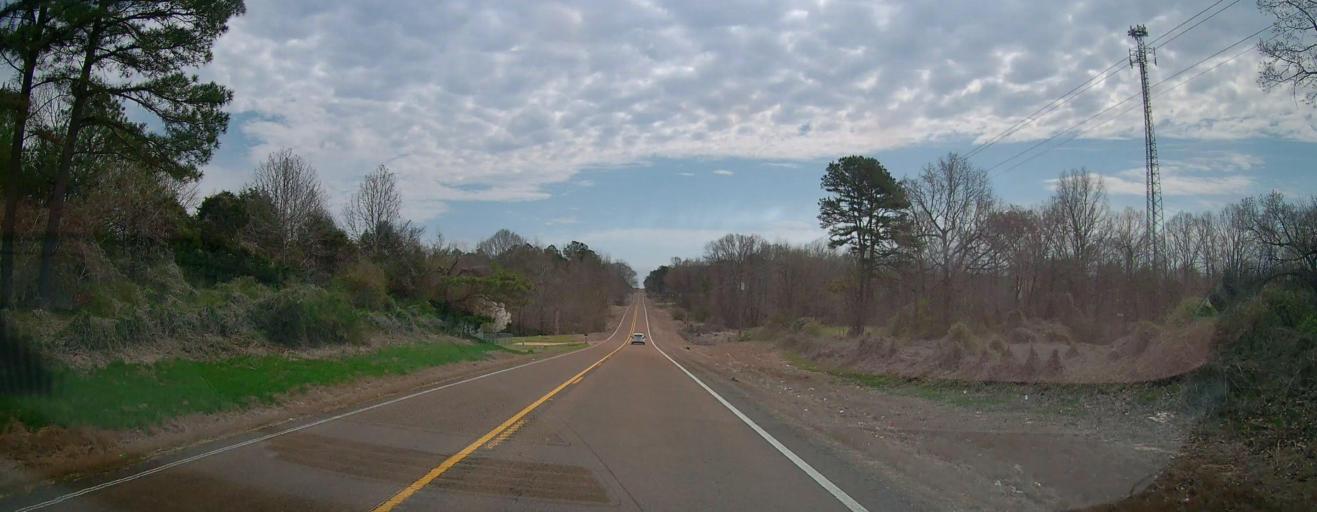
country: US
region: Mississippi
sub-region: Marshall County
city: Holly Springs
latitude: 34.8208
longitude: -89.5431
